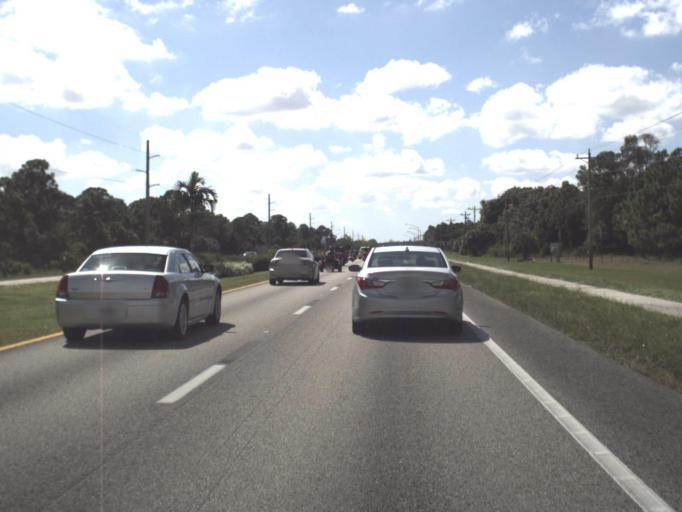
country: US
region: Florida
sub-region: Lee County
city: Palmona Park
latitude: 26.6953
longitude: -81.9010
